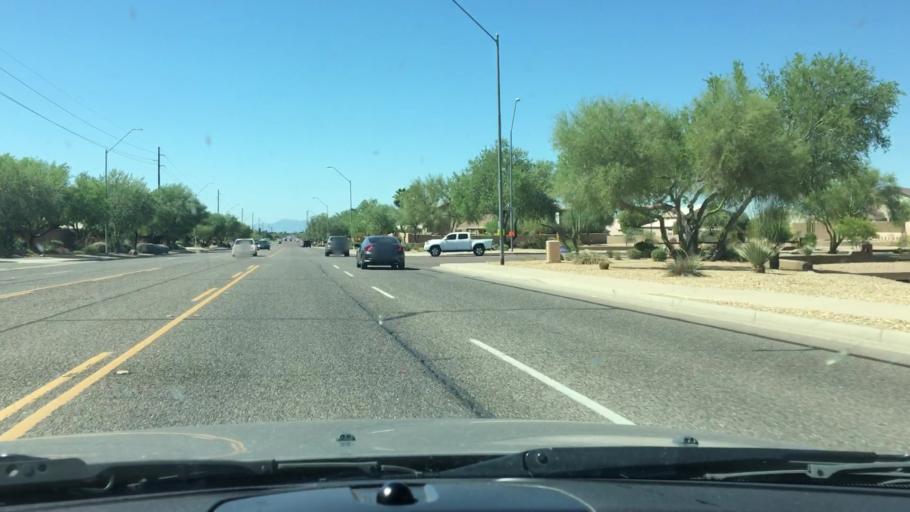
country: US
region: Arizona
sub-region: Maricopa County
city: Sun City
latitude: 33.7185
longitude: -112.2032
